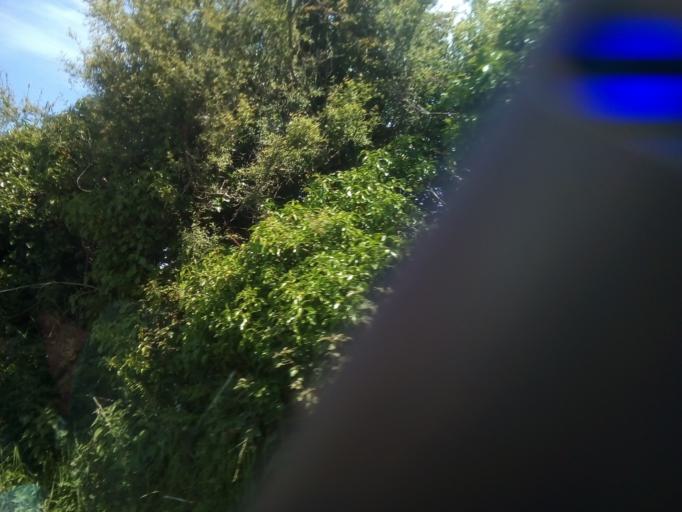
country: IE
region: Leinster
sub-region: Loch Garman
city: Loch Garman
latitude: 52.2432
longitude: -6.6040
